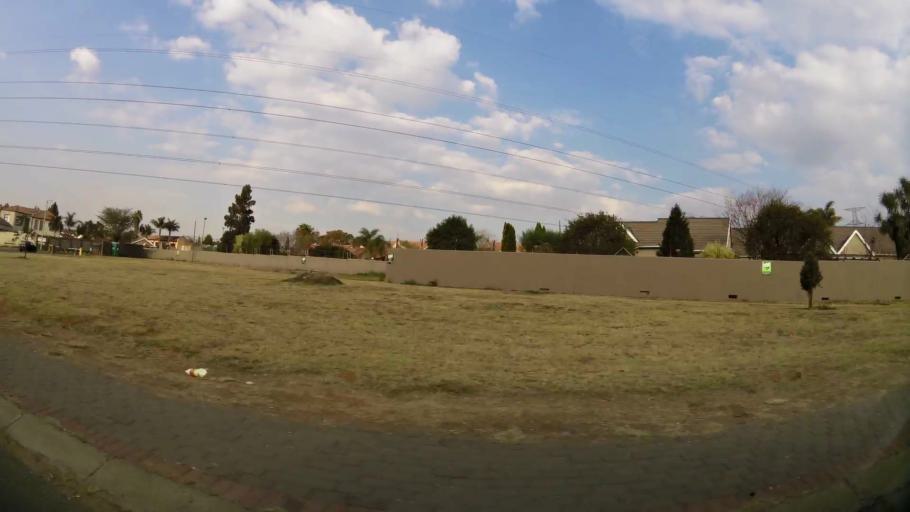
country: ZA
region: Gauteng
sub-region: City of Johannesburg Metropolitan Municipality
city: Modderfontein
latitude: -26.1333
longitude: 28.1834
